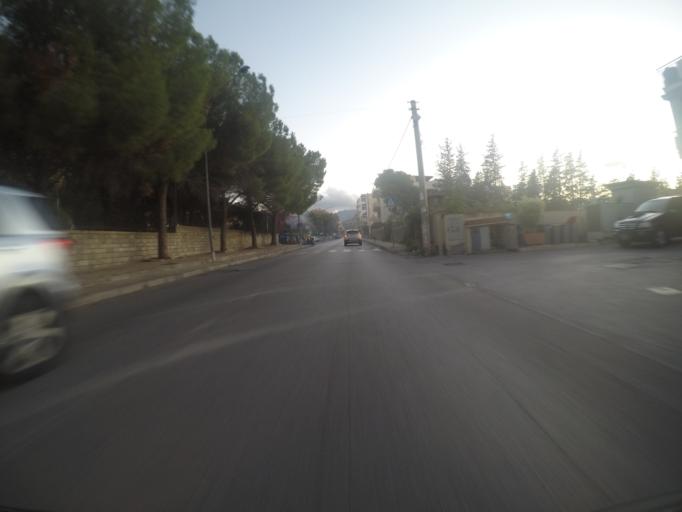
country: IT
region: Sicily
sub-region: Palermo
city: Capaci
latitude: 38.1778
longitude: 13.2436
